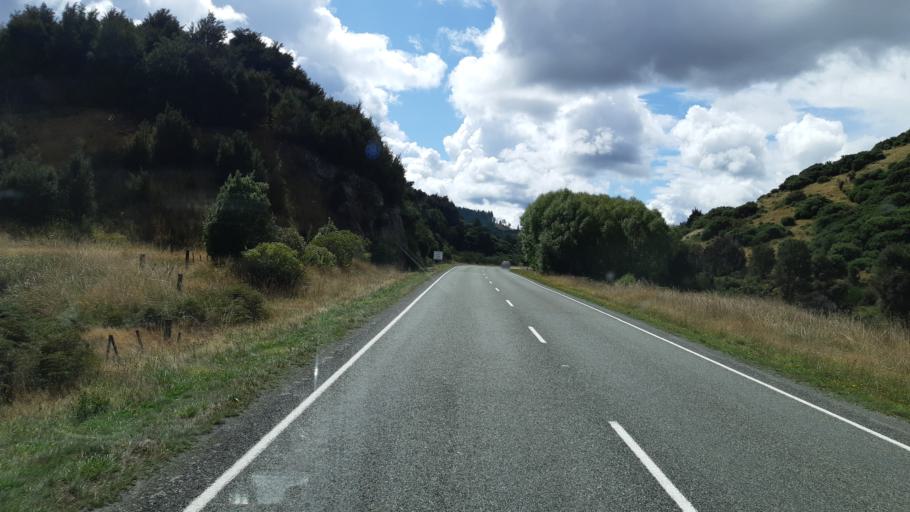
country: NZ
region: Tasman
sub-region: Tasman District
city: Wakefield
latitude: -41.6469
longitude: 172.6541
